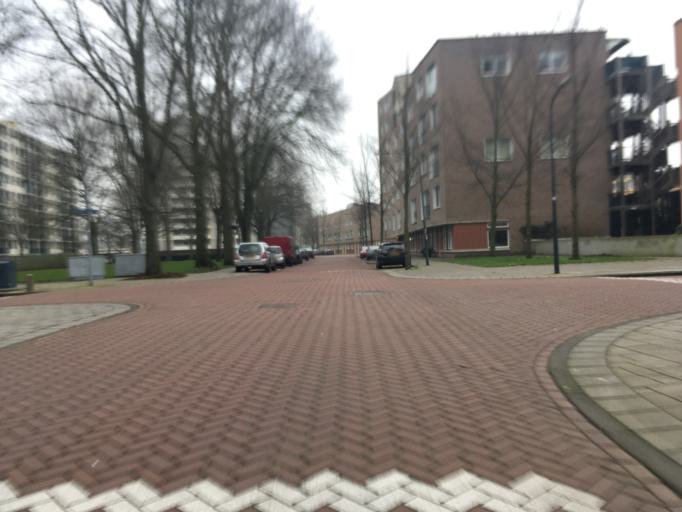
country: NL
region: North Holland
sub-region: Gemeente Haarlem
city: Haarlem
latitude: 52.3660
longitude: 4.6463
